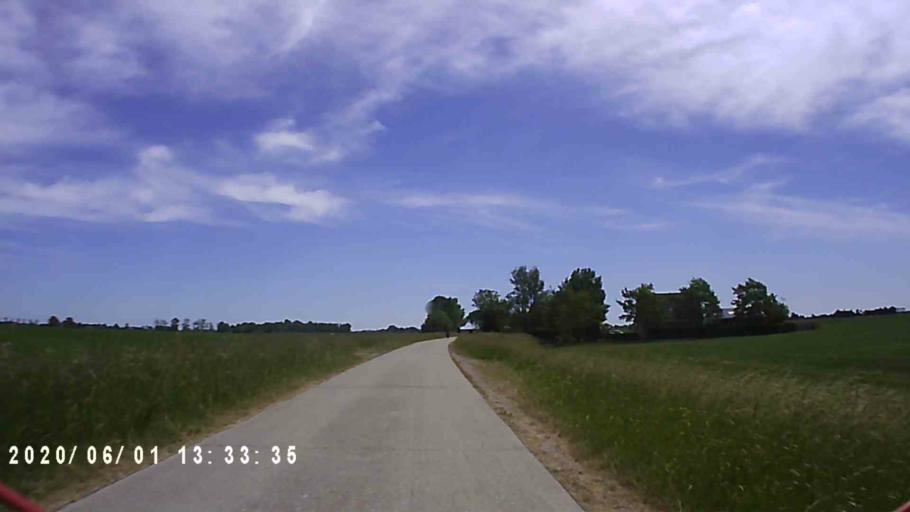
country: NL
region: Friesland
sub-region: Gemeente Littenseradiel
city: Wommels
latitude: 53.0908
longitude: 5.5706
